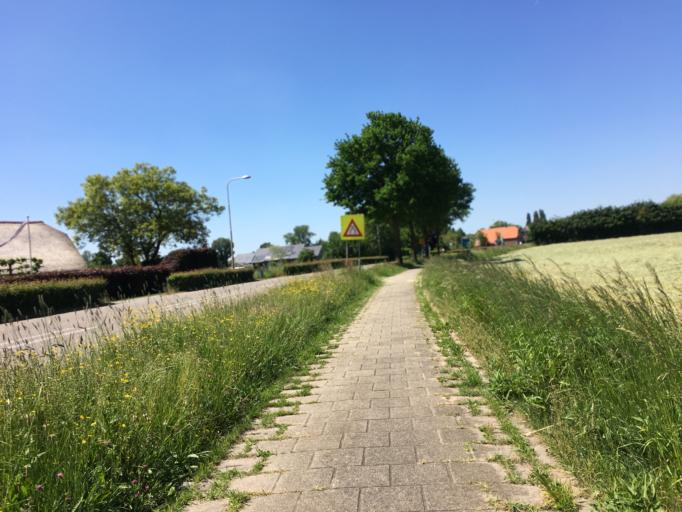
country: NL
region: North Brabant
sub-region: Gemeente Heusden
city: Heusden
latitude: 51.7304
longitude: 5.1630
